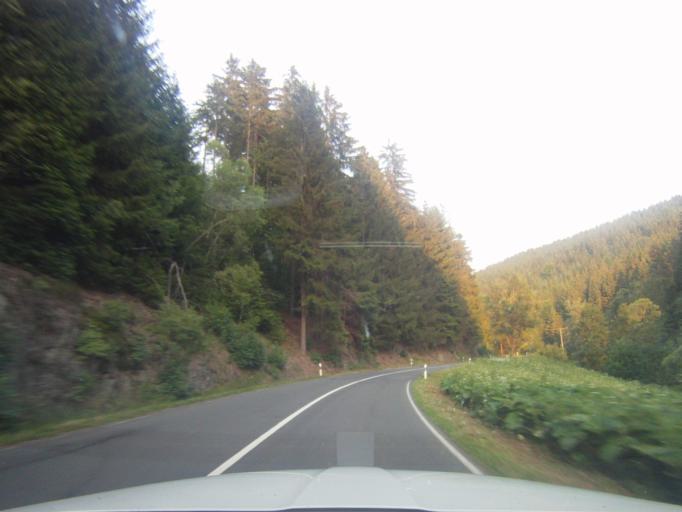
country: DE
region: Thuringia
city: Eisfeld
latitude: 50.4846
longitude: 10.8949
